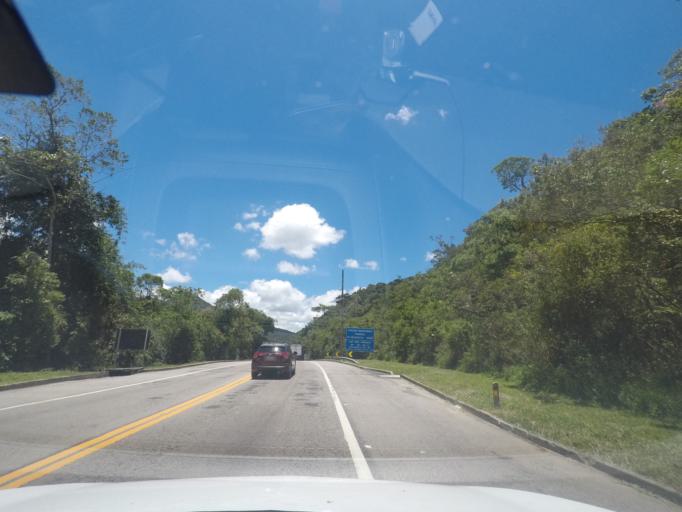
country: BR
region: Rio de Janeiro
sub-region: Teresopolis
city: Teresopolis
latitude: -22.4611
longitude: -42.9818
